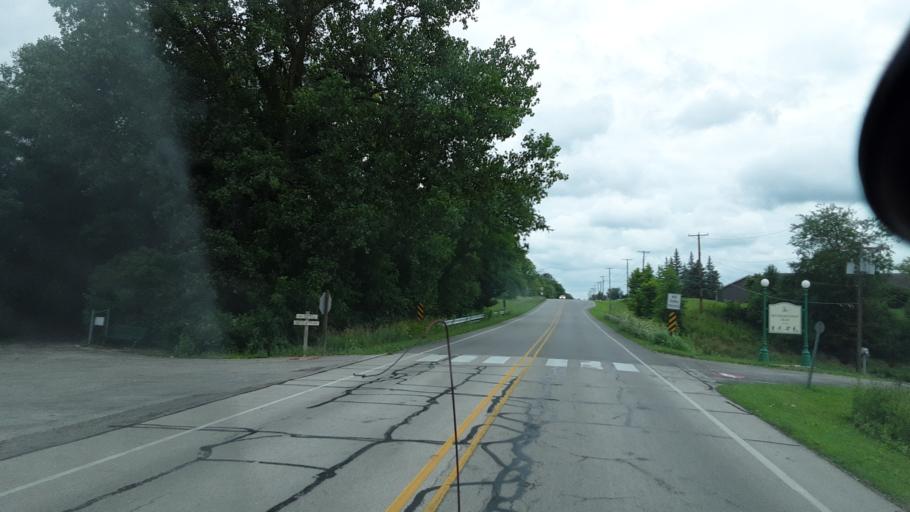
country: US
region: Indiana
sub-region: Adams County
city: Decatur
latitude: 40.8163
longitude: -84.9096
